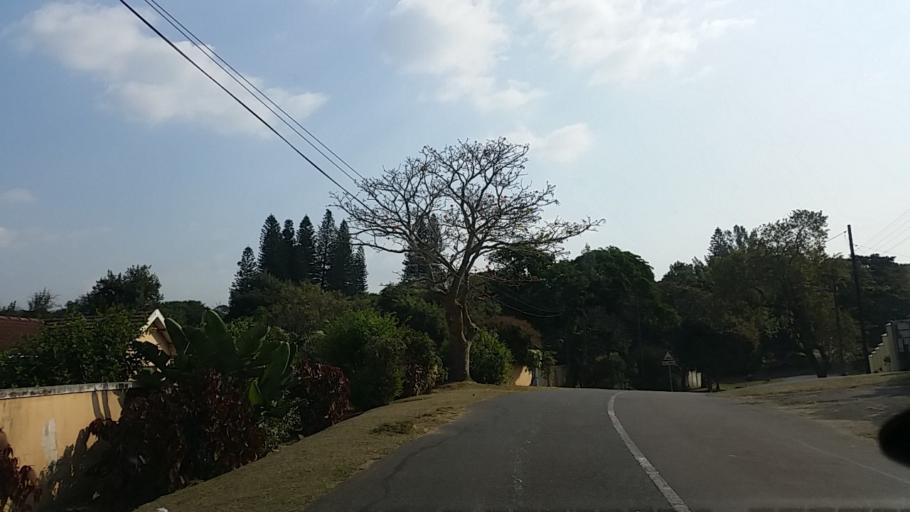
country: ZA
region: KwaZulu-Natal
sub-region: eThekwini Metropolitan Municipality
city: Berea
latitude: -29.8392
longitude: 30.9431
